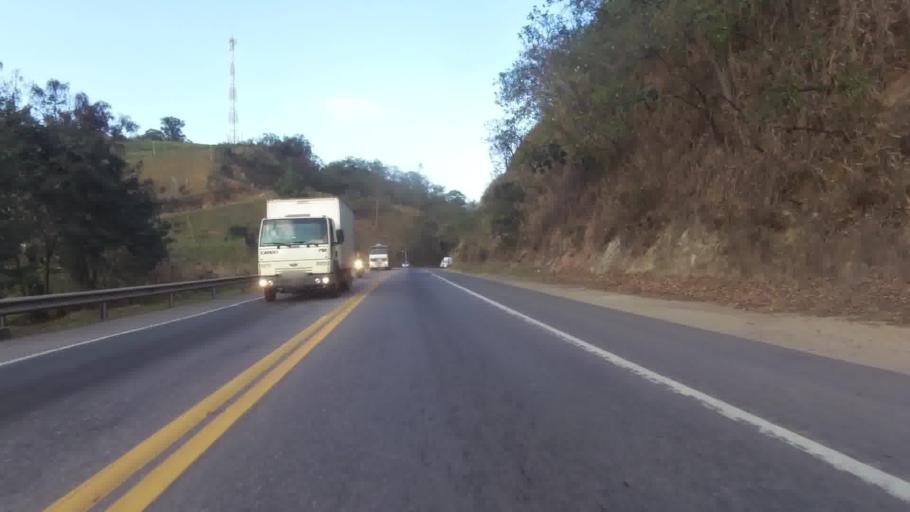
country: BR
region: Espirito Santo
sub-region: Rio Novo Do Sul
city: Rio Novo do Sul
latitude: -20.8656
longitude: -40.9299
